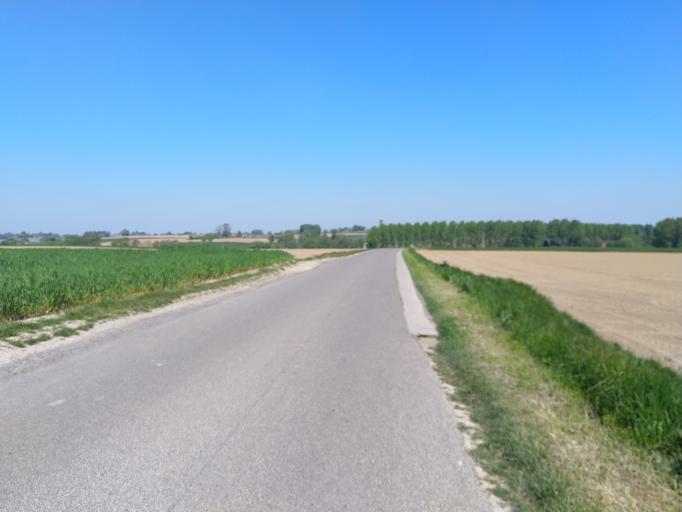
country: BE
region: Wallonia
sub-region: Province du Hainaut
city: Enghien
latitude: 50.6173
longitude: 4.0113
